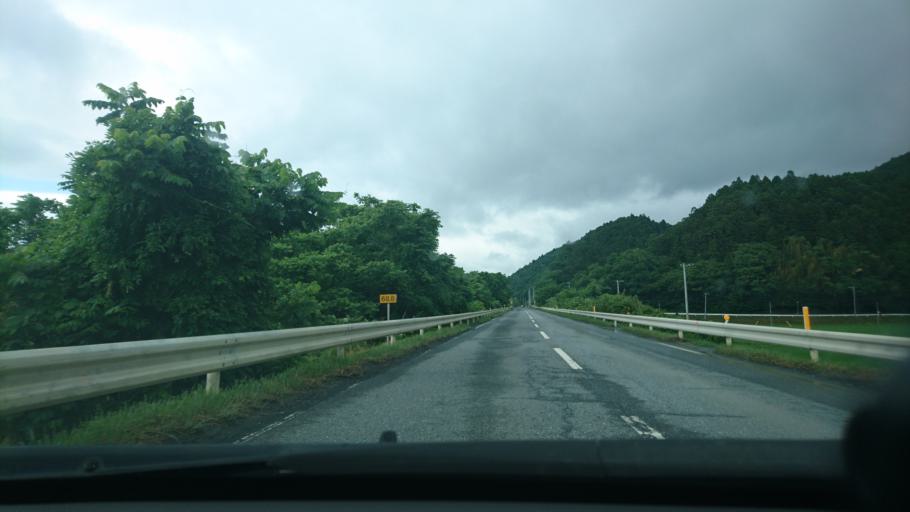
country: JP
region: Miyagi
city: Ishinomaki
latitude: 38.5632
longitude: 141.2995
